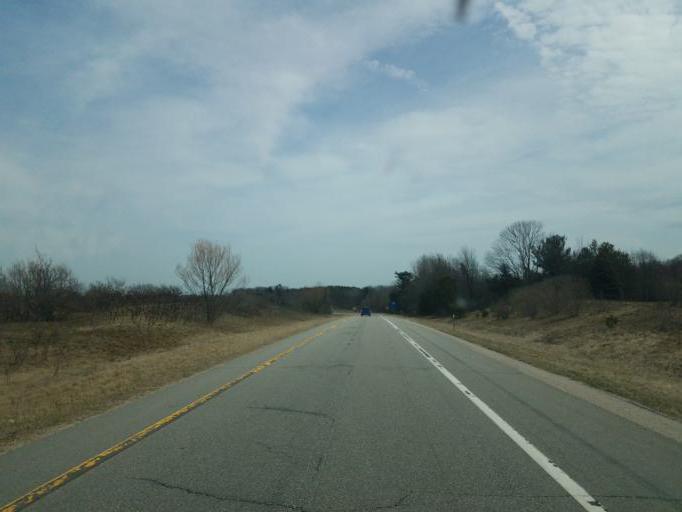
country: US
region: Michigan
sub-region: Mason County
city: Ludington
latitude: 43.9130
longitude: -86.4079
